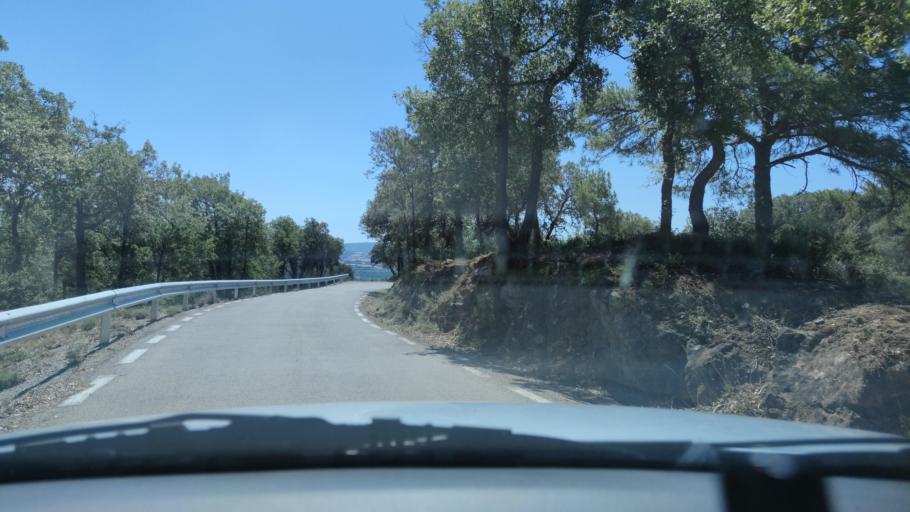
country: ES
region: Catalonia
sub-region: Provincia de Lleida
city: Tora de Riubregos
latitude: 41.8574
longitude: 1.4350
